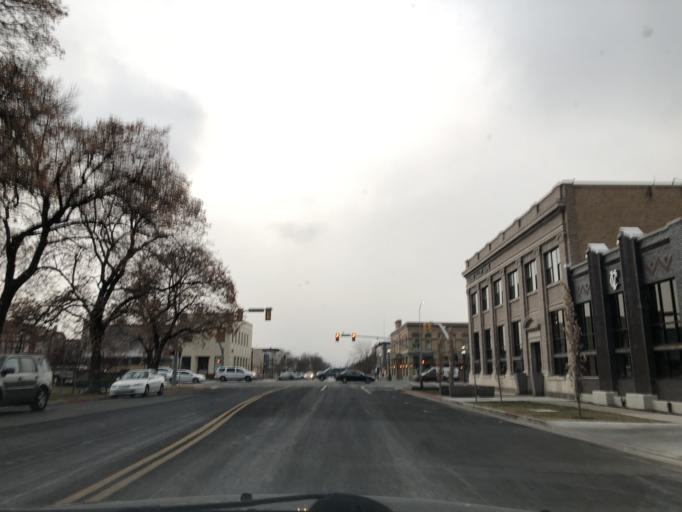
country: US
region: Utah
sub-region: Cache County
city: Logan
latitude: 41.7333
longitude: -111.8340
